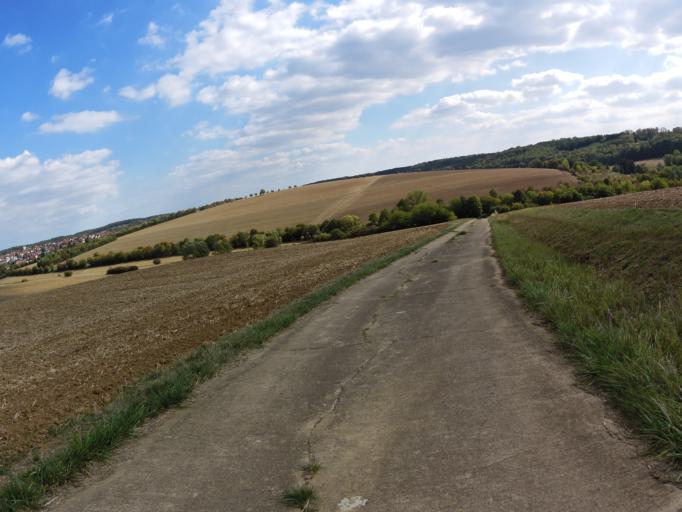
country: DE
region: Bavaria
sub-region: Regierungsbezirk Unterfranken
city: Hettstadt
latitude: 49.7853
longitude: 9.8139
